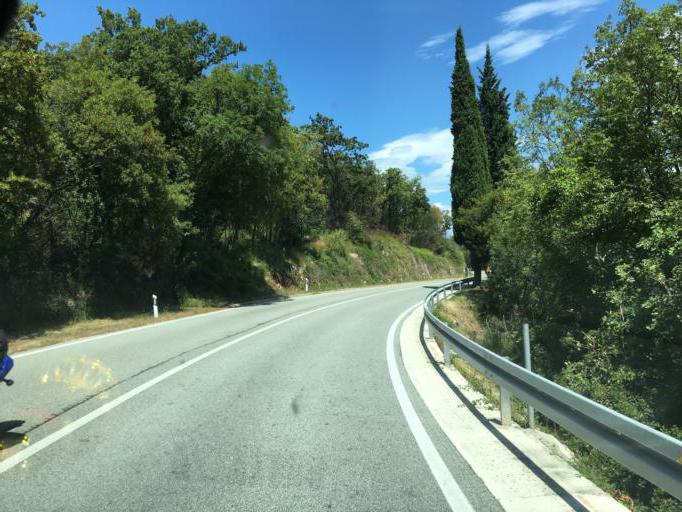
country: HR
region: Istarska
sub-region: Grad Labin
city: Rabac
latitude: 45.1335
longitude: 14.2049
